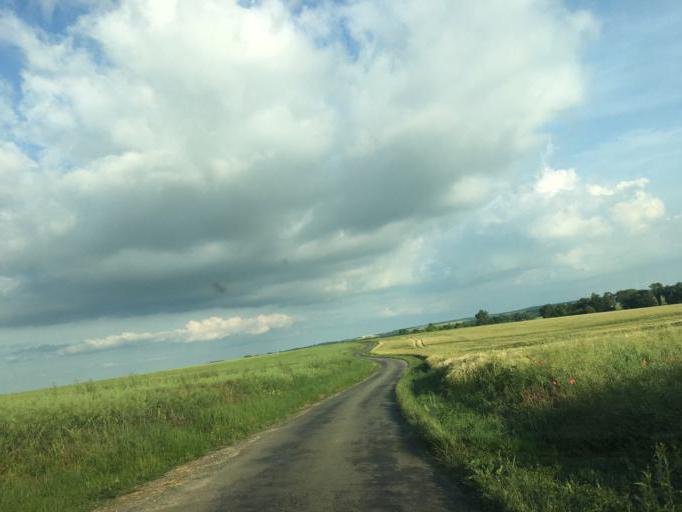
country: FR
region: Poitou-Charentes
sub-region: Departement des Deux-Sevres
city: Mauze-sur-le-Mignon
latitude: 46.0839
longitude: -0.5803
